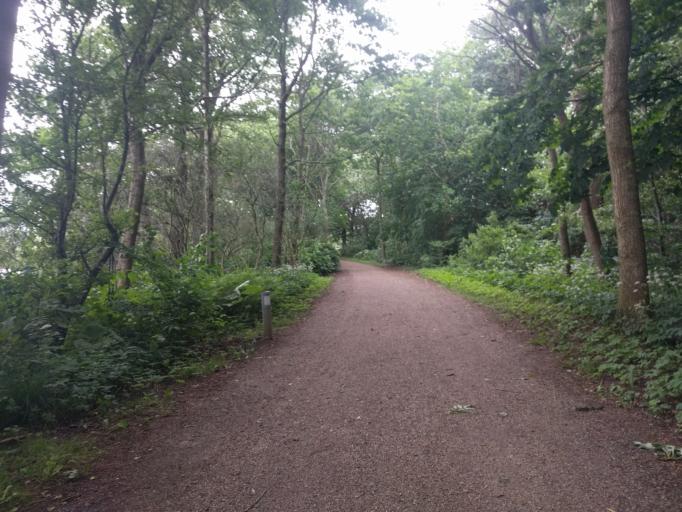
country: DK
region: Central Jutland
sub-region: Viborg Kommune
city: Viborg
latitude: 56.4631
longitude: 9.4204
